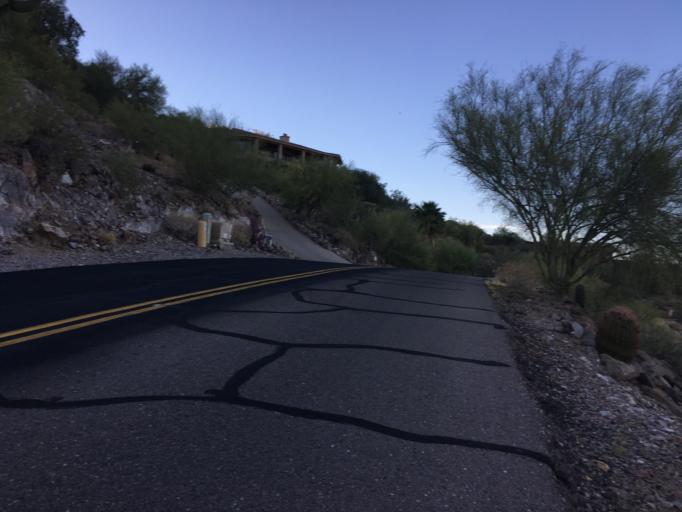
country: US
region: Arizona
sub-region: Maricopa County
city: Paradise Valley
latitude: 33.5398
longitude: -111.9856
